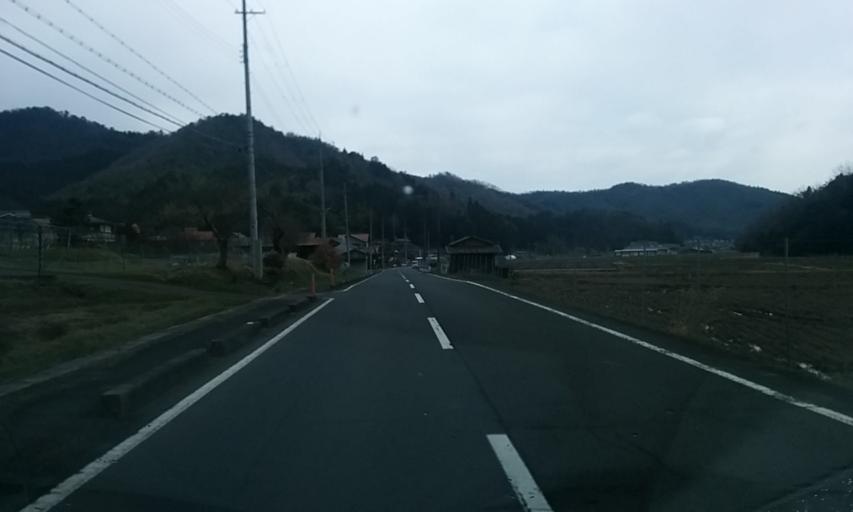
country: JP
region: Hyogo
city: Sasayama
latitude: 35.1279
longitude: 135.4117
